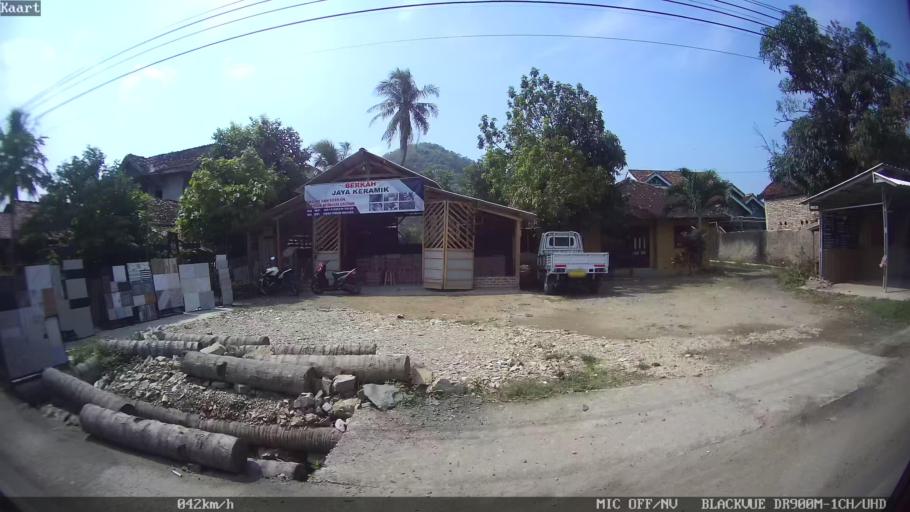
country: ID
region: Lampung
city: Gadingrejo
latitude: -5.3828
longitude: 105.0200
